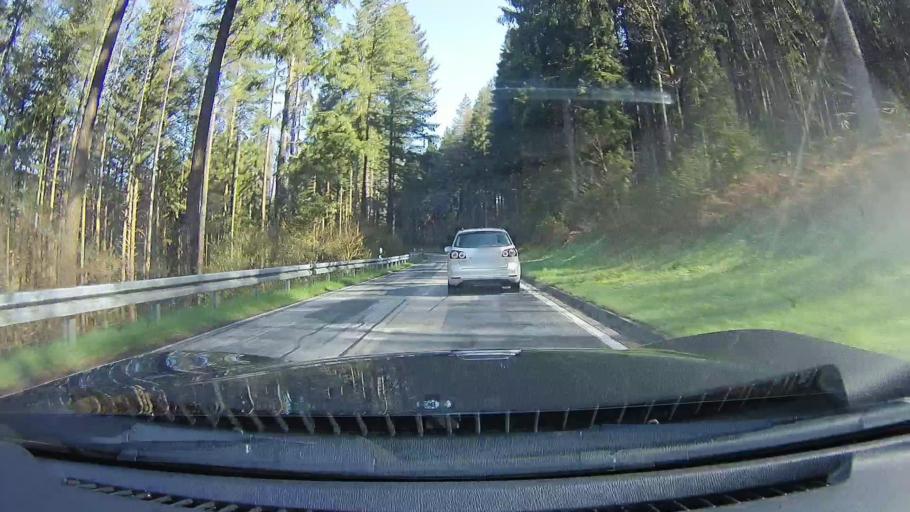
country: DE
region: Hesse
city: Hirschhorn
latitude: 49.4705
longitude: 8.9013
